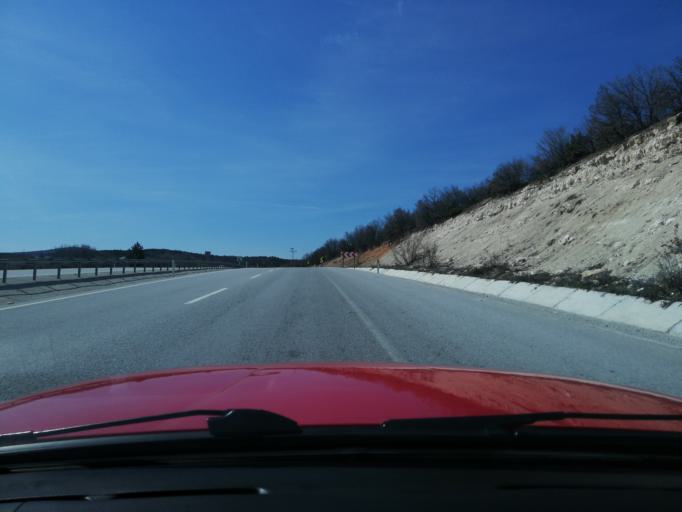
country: TR
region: Kuetahya
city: Kutahya
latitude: 39.3618
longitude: 30.0598
